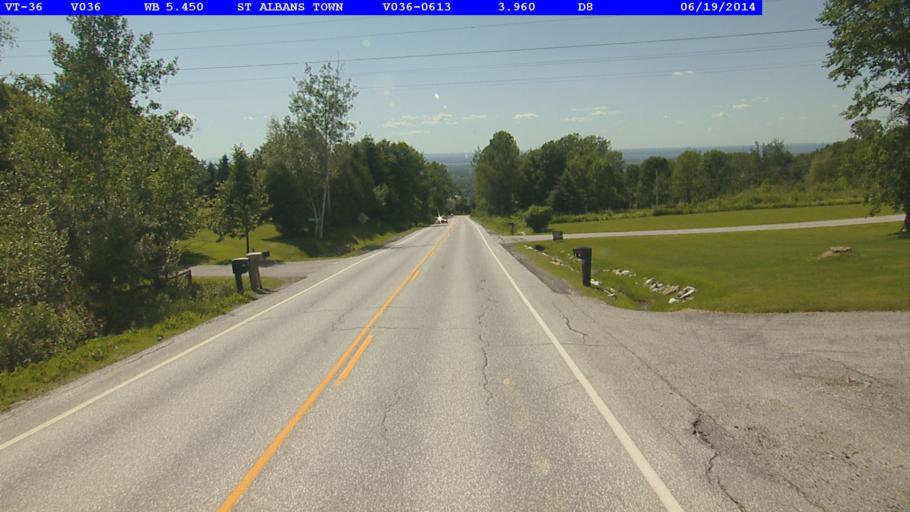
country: US
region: Vermont
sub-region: Franklin County
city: Saint Albans
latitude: 44.7977
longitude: -73.0538
